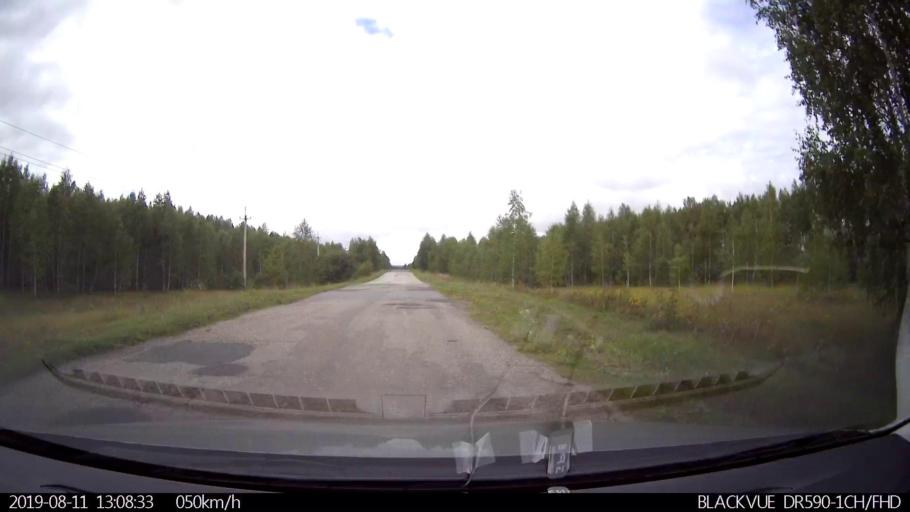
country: RU
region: Ulyanovsk
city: Ignatovka
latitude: 53.8589
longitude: 47.6324
